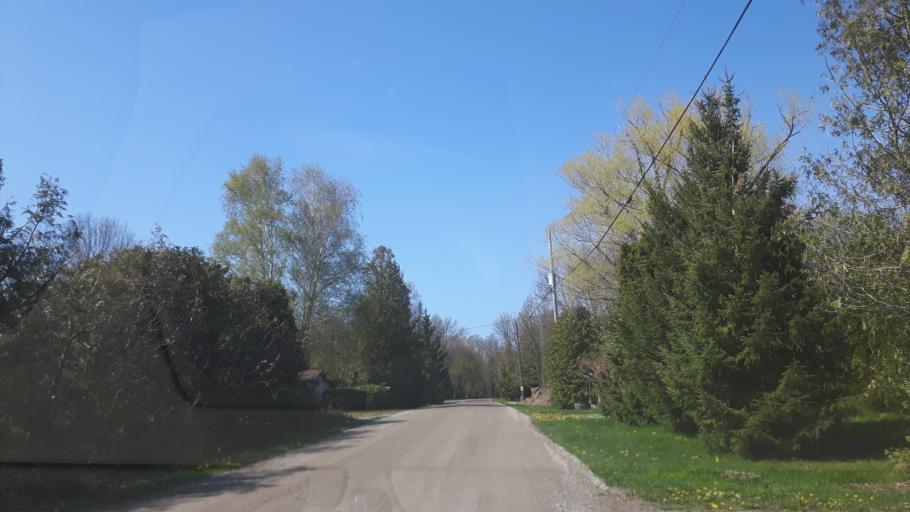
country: CA
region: Ontario
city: Bluewater
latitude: 43.5437
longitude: -81.7052
